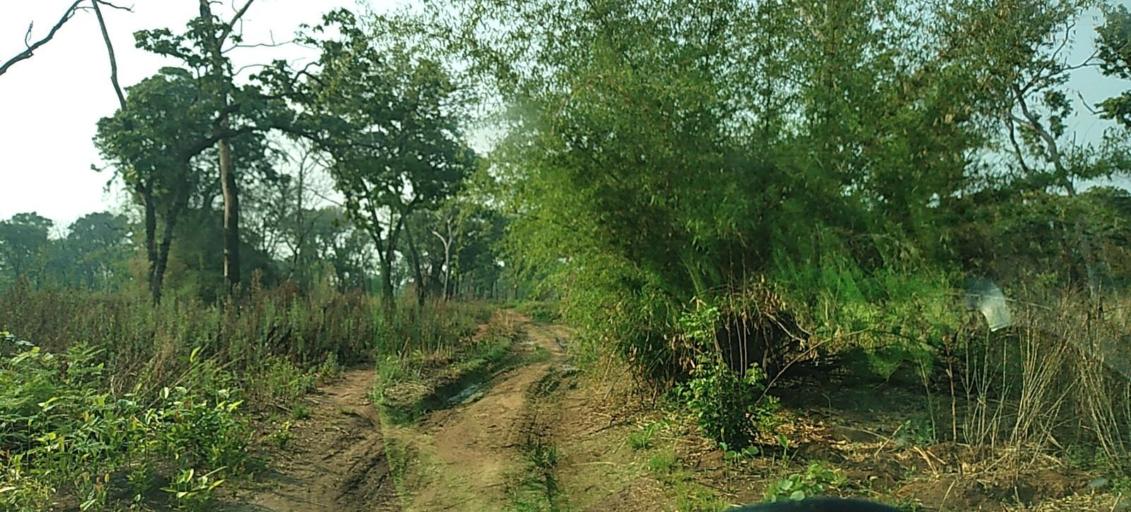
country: ZM
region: North-Western
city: Solwezi
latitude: -12.4030
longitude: 26.5863
